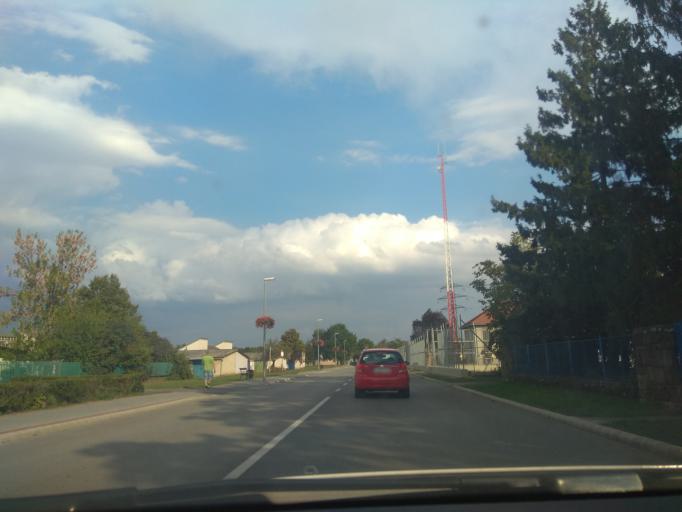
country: HU
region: Borsod-Abauj-Zemplen
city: Sajooeroes
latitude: 47.9299
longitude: 21.0455
